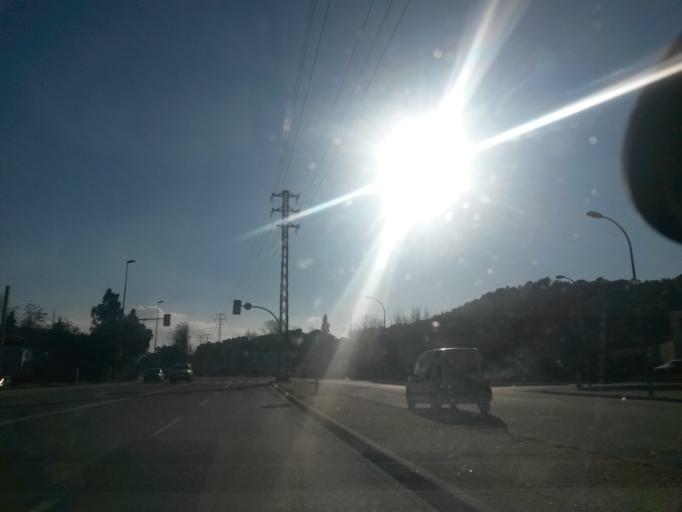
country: ES
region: Catalonia
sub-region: Provincia de Girona
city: Sarria de Ter
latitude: 42.0038
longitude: 2.8160
